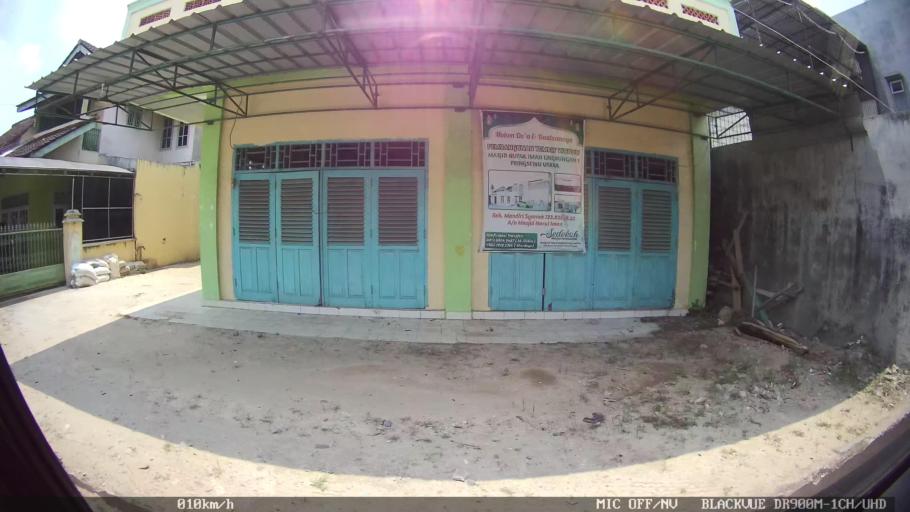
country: ID
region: Lampung
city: Pringsewu
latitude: -5.3577
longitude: 104.9879
